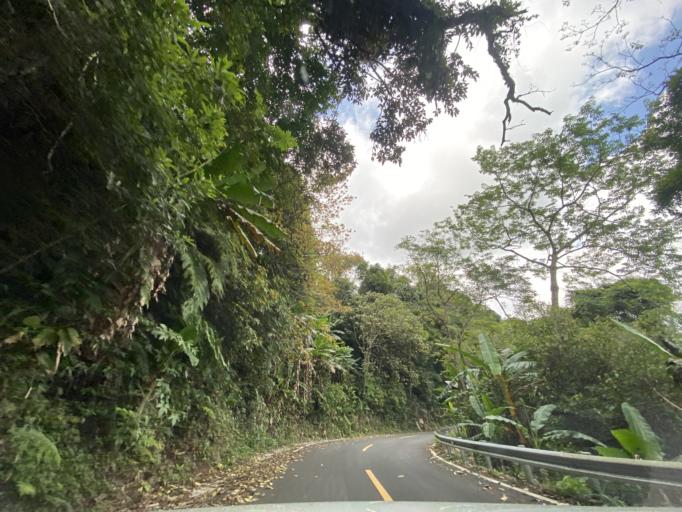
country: CN
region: Hainan
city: Diaoluoshan
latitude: 18.7062
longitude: 109.8823
